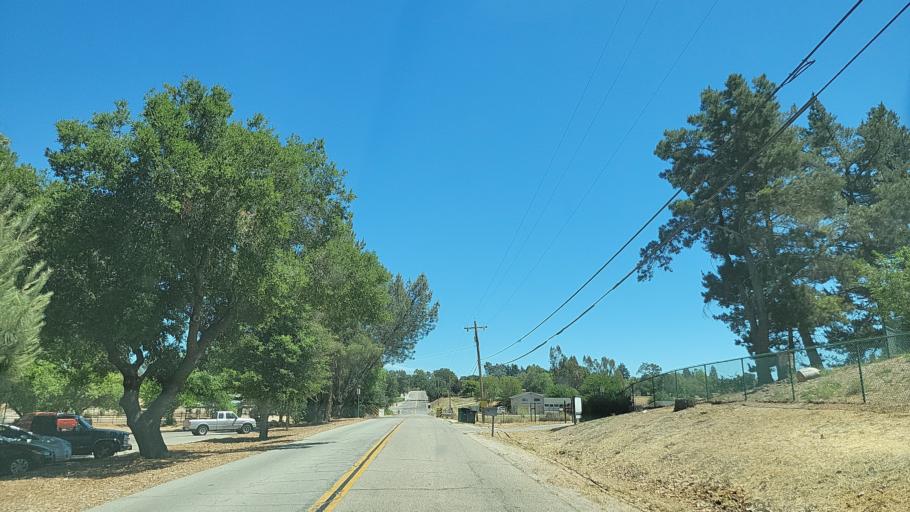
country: US
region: California
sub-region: San Luis Obispo County
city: Atascadero
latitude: 35.4528
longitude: -120.6349
